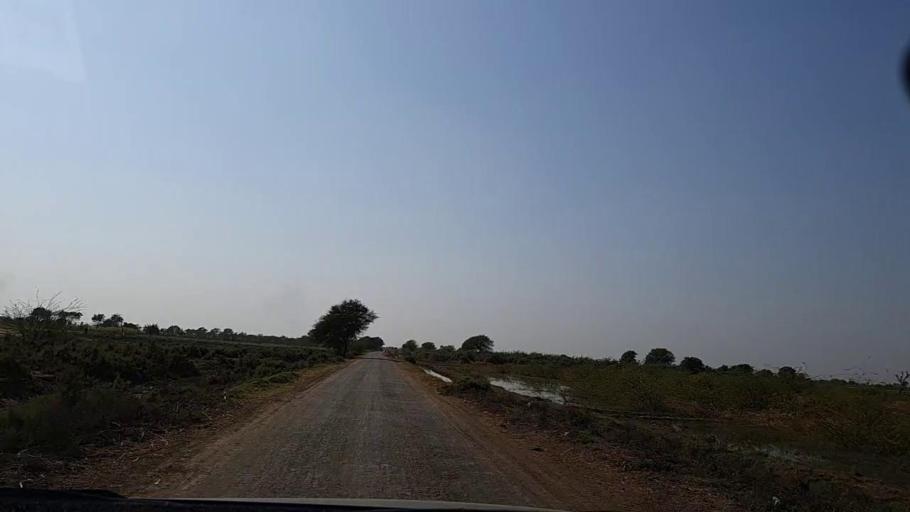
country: PK
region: Sindh
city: Digri
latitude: 25.1736
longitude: 69.0587
